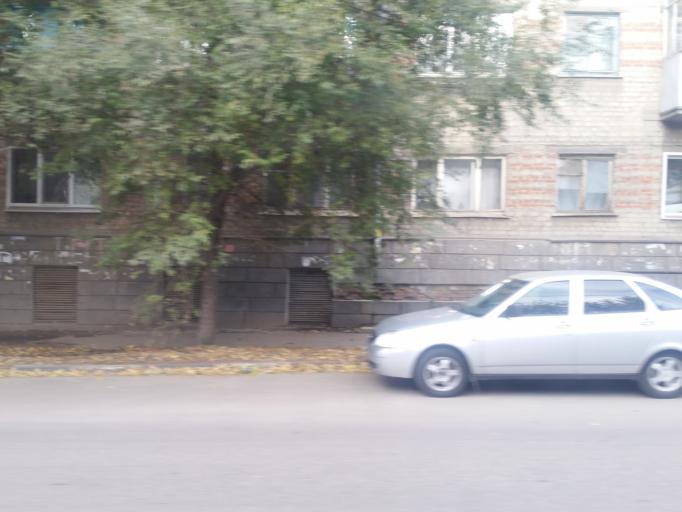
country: RU
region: Ulyanovsk
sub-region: Ulyanovskiy Rayon
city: Ulyanovsk
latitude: 54.3203
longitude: 48.3903
